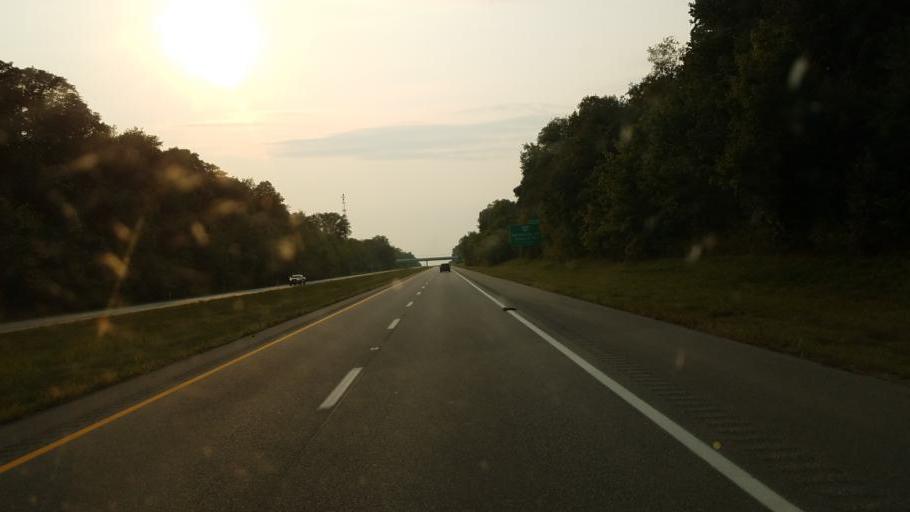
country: US
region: Ohio
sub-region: Geauga County
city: Bainbridge
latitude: 41.3849
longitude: -81.3159
